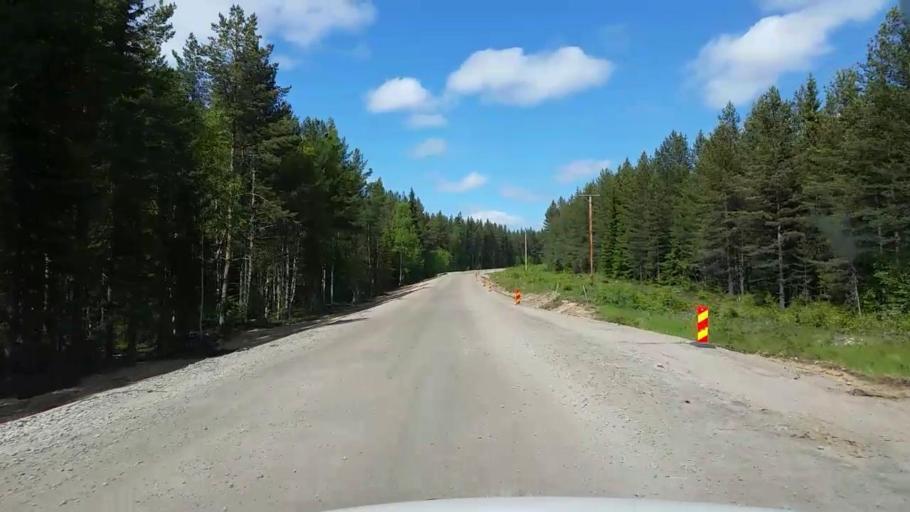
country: SE
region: Gaevleborg
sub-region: Ljusdals Kommun
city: Farila
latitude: 61.5965
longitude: 15.9229
